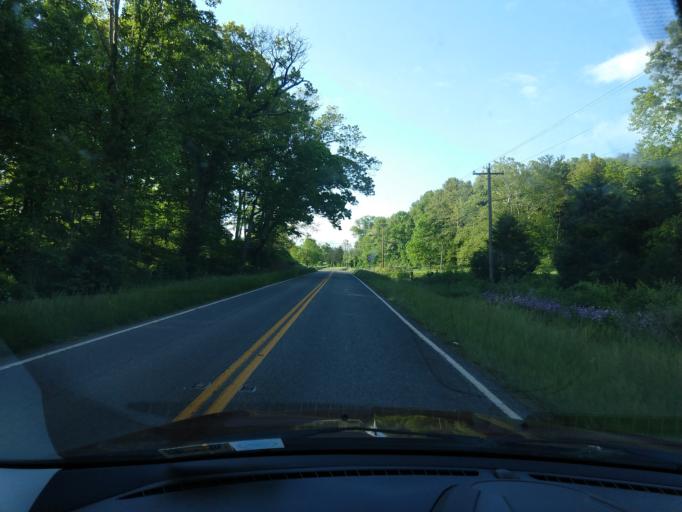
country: US
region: Virginia
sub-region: Wythe County
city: Wytheville
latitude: 36.8425
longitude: -80.9698
